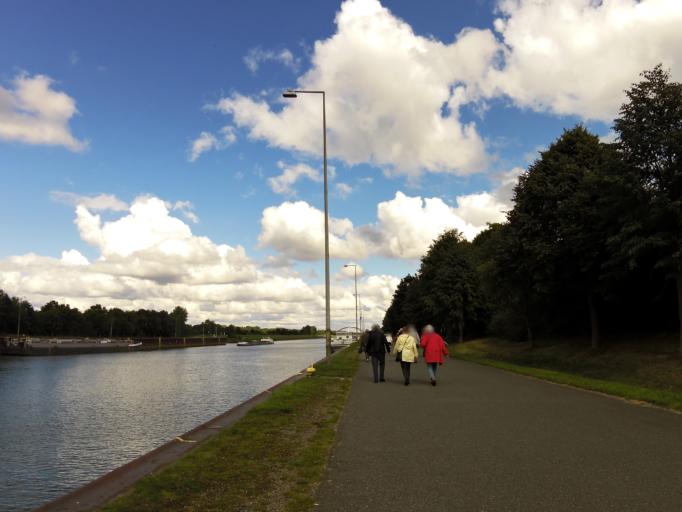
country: DE
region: Lower Saxony
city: Scharnebeck
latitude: 53.2953
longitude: 10.4895
